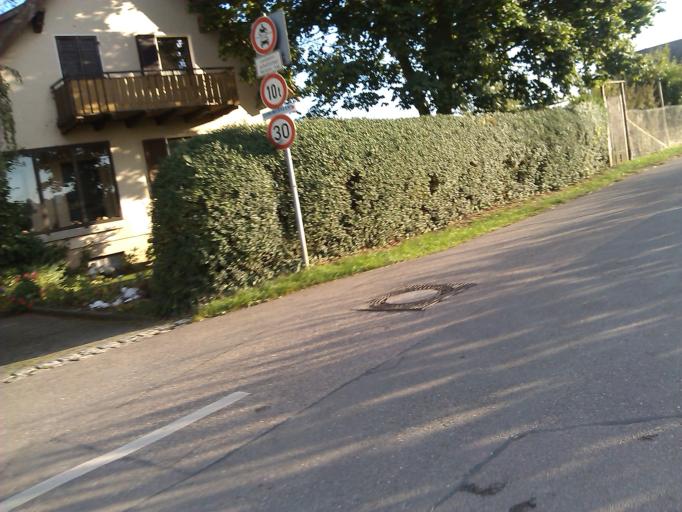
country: DE
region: Baden-Wuerttemberg
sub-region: Regierungsbezirk Stuttgart
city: Nordheim
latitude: 49.1142
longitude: 9.1657
